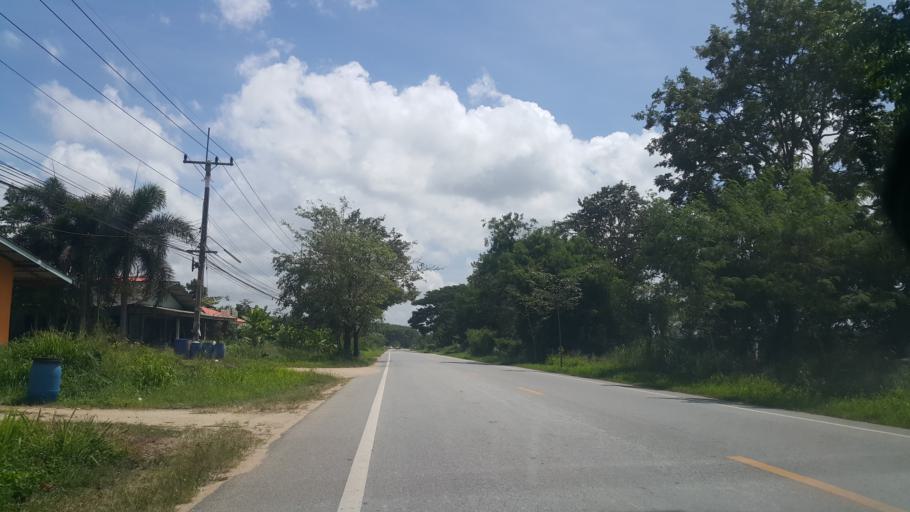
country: TH
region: Rayong
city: Ban Chang
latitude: 12.7952
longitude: 101.0439
